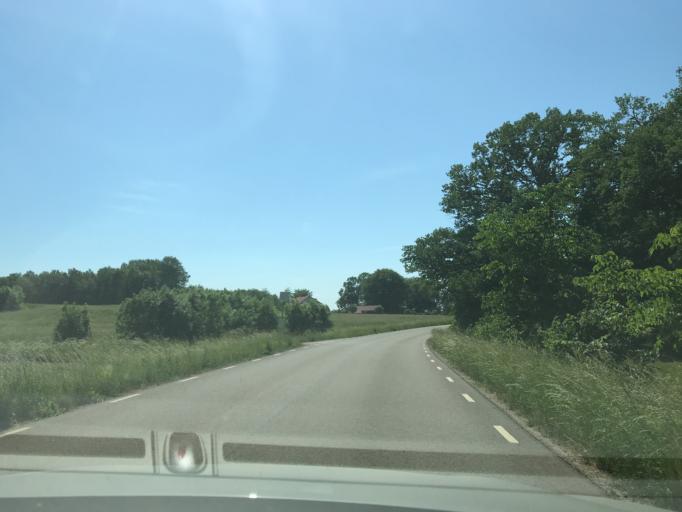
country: SE
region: Vaestra Goetaland
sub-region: Gotene Kommun
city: Kallby
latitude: 58.5424
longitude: 13.3293
